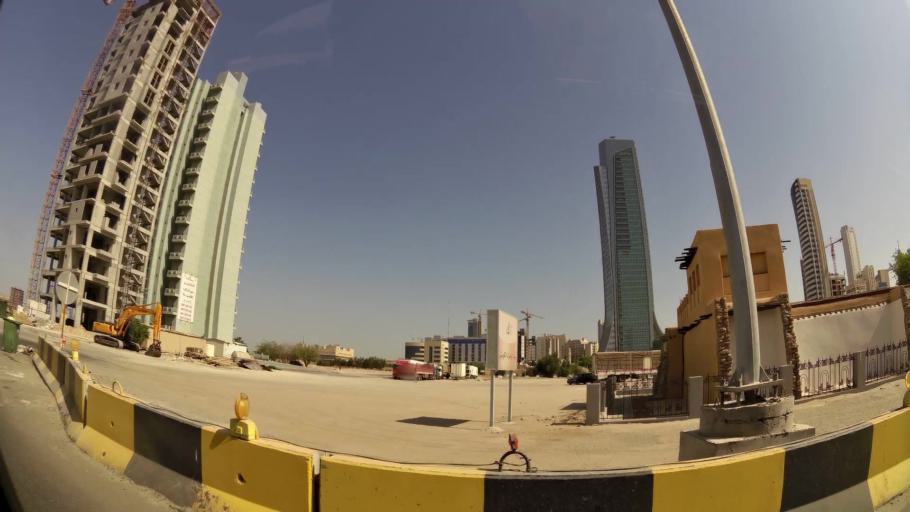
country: KW
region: Al Asimah
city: Kuwait City
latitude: 29.3850
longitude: 47.9837
